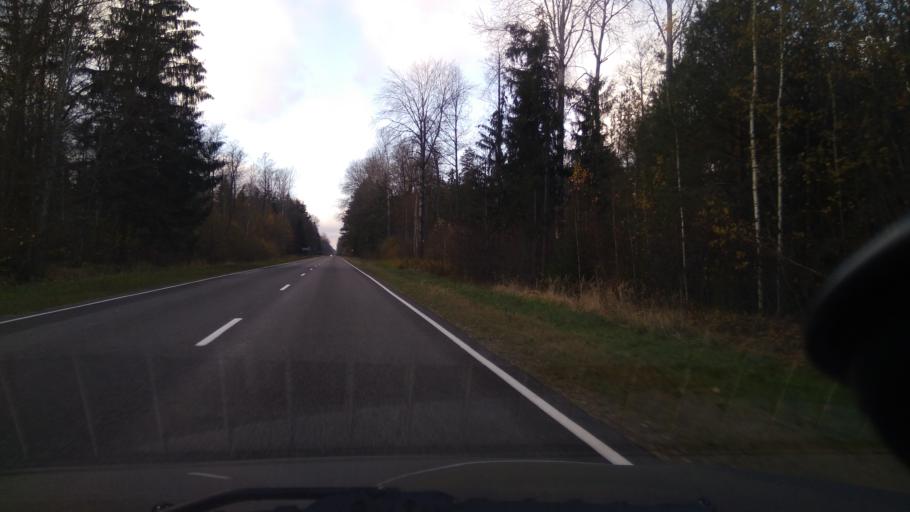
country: BY
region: Minsk
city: Urechcha
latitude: 53.2088
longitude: 27.9081
